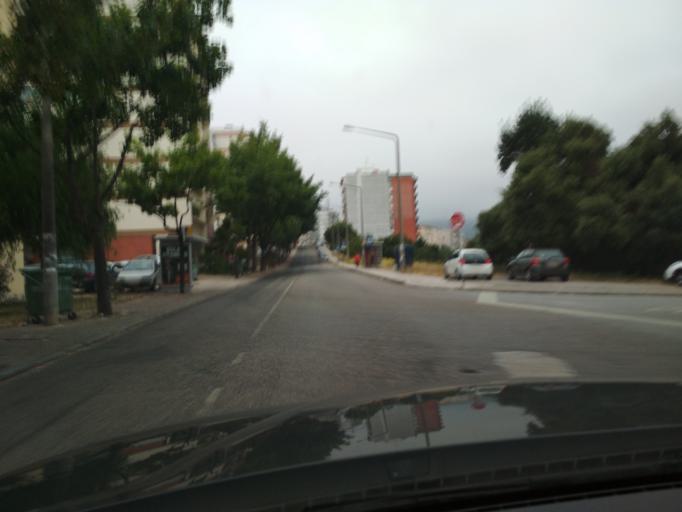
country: PT
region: Coimbra
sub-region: Coimbra
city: Coimbra
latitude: 40.1958
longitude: -8.4151
